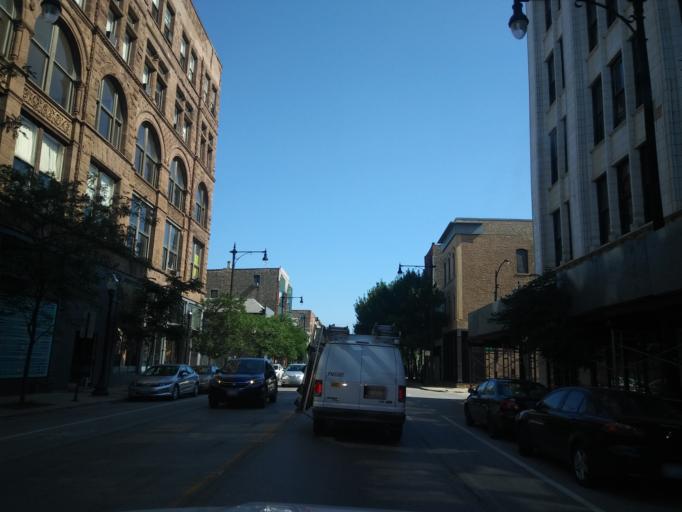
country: US
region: Illinois
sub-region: Cook County
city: Chicago
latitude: 41.8558
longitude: -87.6466
